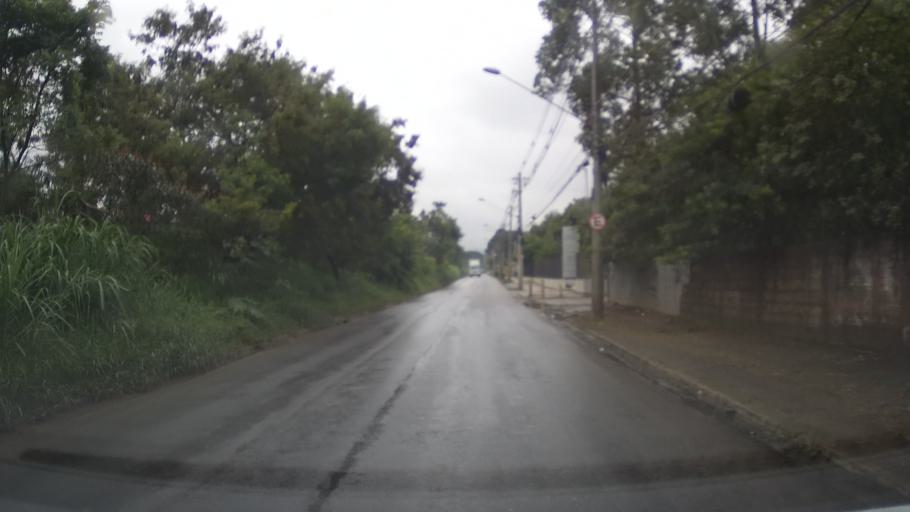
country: BR
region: Sao Paulo
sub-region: Guarulhos
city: Guarulhos
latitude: -23.4756
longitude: -46.4585
